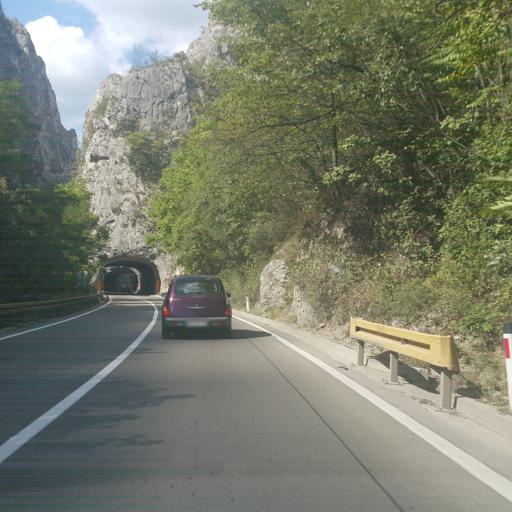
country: RS
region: Central Serbia
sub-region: Nisavski Okrug
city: Svrljig
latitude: 43.3263
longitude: 22.1631
